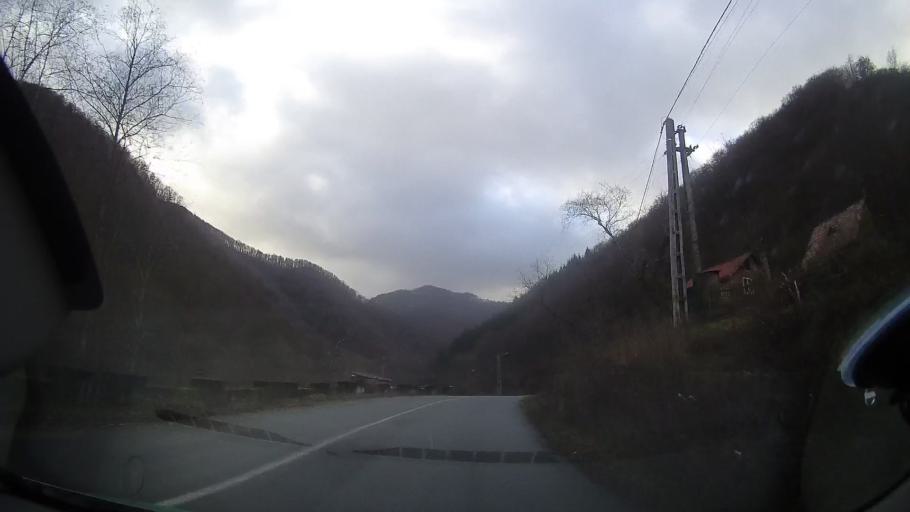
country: RO
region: Cluj
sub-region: Comuna Maguri-Racatau
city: Maguri-Racatau
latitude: 46.6739
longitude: 23.2546
